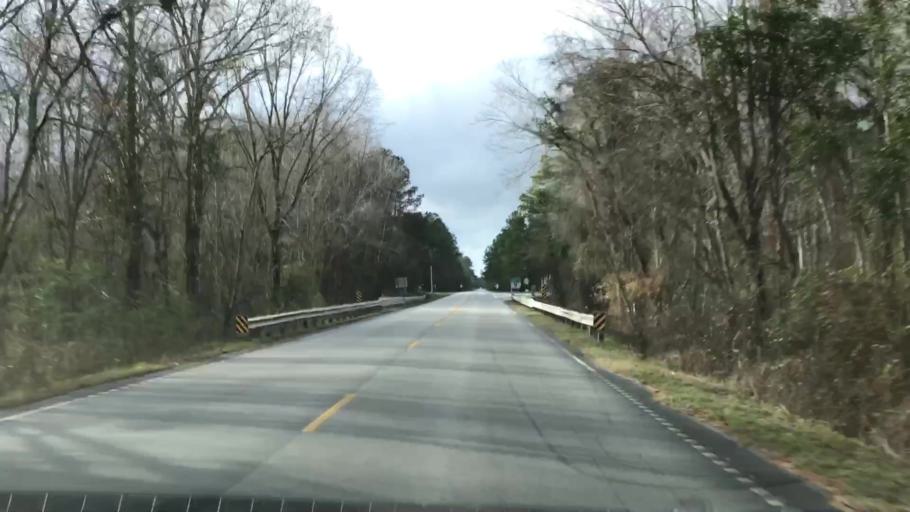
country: US
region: South Carolina
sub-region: Berkeley County
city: Saint Stephen
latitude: 33.2863
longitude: -79.7554
